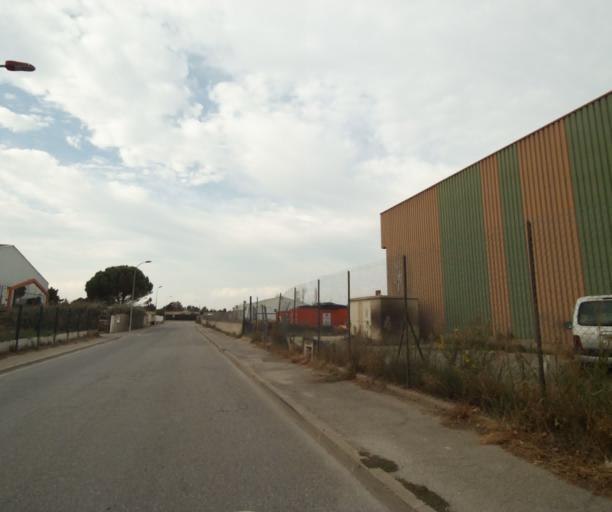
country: FR
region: Provence-Alpes-Cote d'Azur
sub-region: Departement des Bouches-du-Rhone
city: Marignane
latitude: 43.4072
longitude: 5.2019
